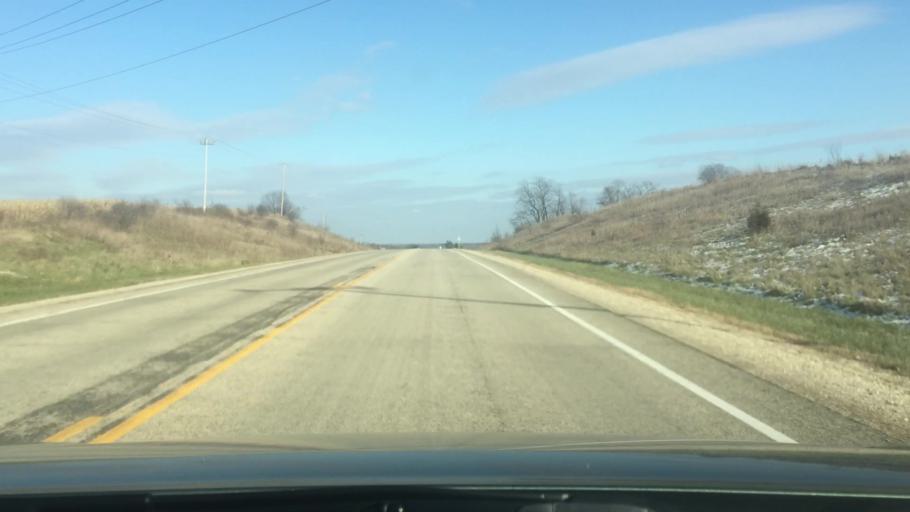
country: US
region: Wisconsin
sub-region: Jefferson County
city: Palmyra
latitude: 42.9335
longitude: -88.6435
